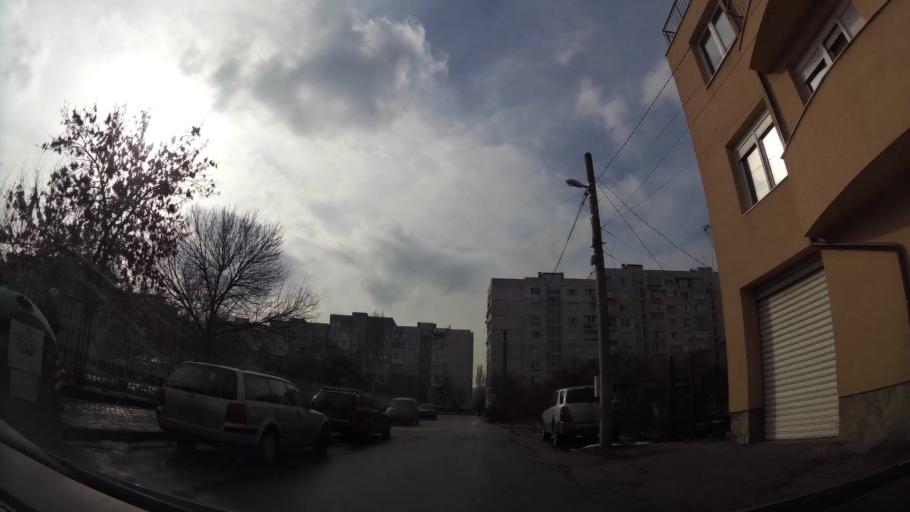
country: BG
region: Sofia-Capital
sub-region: Stolichna Obshtina
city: Sofia
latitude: 42.7180
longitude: 23.2742
